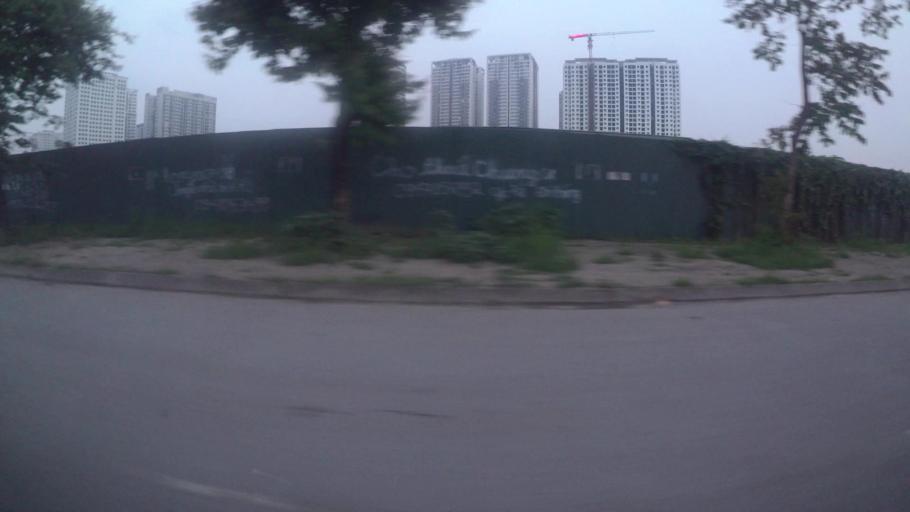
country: VN
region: Ha Noi
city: Tay Ho
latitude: 21.0667
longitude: 105.7946
